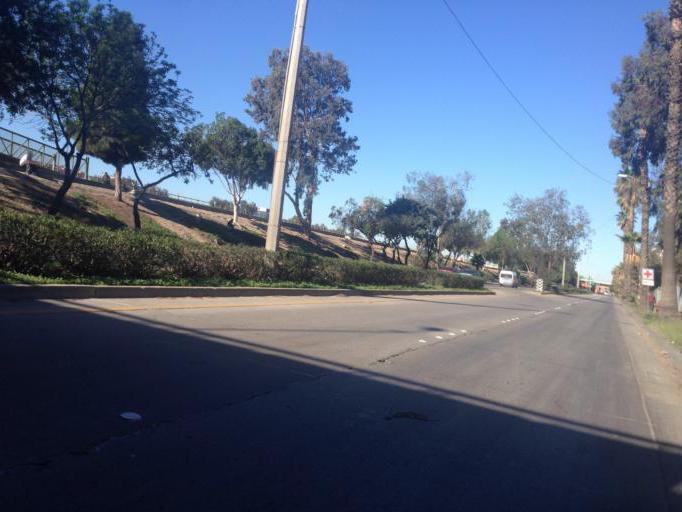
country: MX
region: Baja California
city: Tijuana
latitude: 32.5258
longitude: -117.0112
